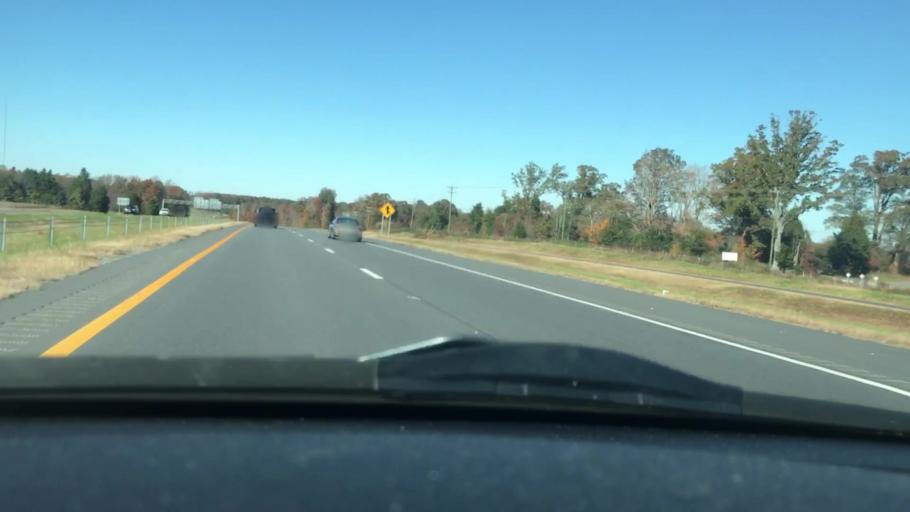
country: US
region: North Carolina
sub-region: Guilford County
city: Summerfield
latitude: 36.2477
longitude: -79.9210
